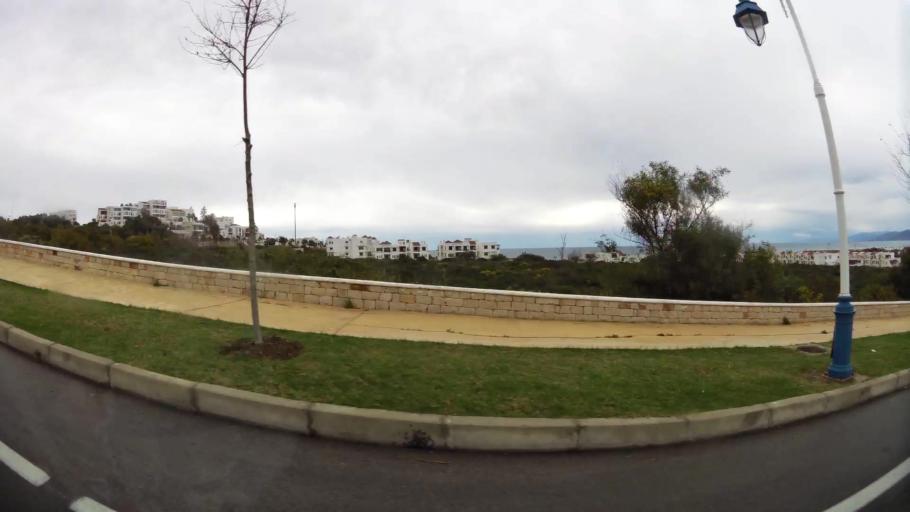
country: MA
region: Tanger-Tetouan
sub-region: Tetouan
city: Martil
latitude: 35.6644
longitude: -5.2930
